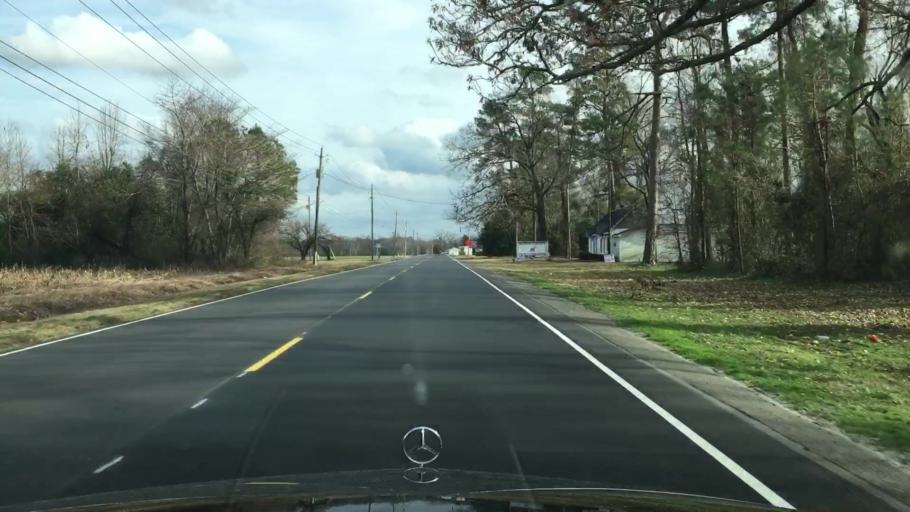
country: US
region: North Carolina
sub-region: Duplin County
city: Kenansville
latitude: 34.9601
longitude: -77.9884
